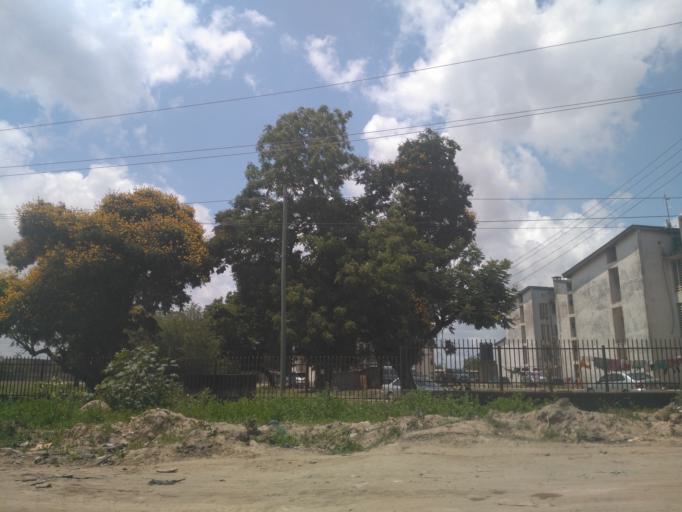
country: TZ
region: Dar es Salaam
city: Dar es Salaam
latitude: -6.8399
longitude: 39.2908
